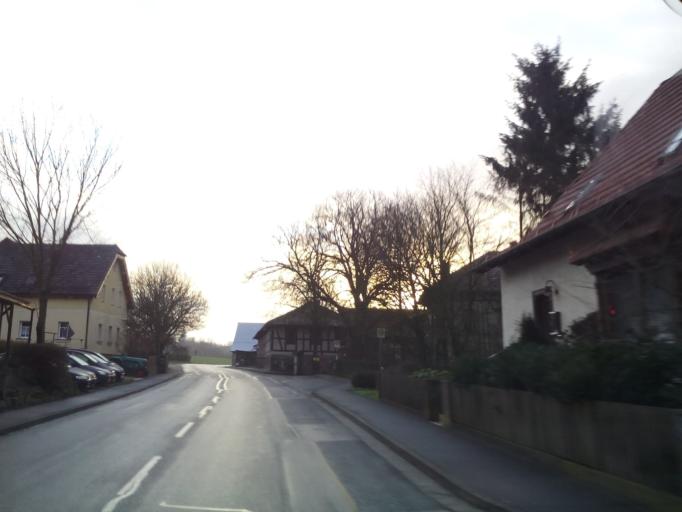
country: DE
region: Bavaria
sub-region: Upper Franconia
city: Untersiemau
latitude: 50.1876
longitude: 10.9974
